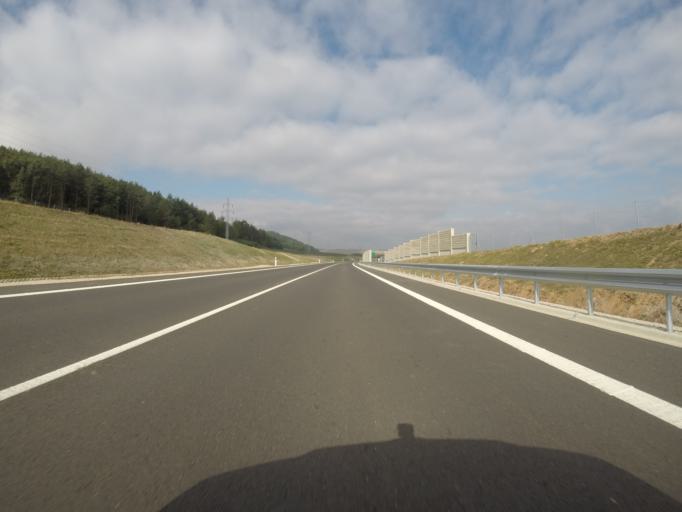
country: SK
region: Nitriansky
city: Banovce nad Bebravou
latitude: 48.7344
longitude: 18.2275
